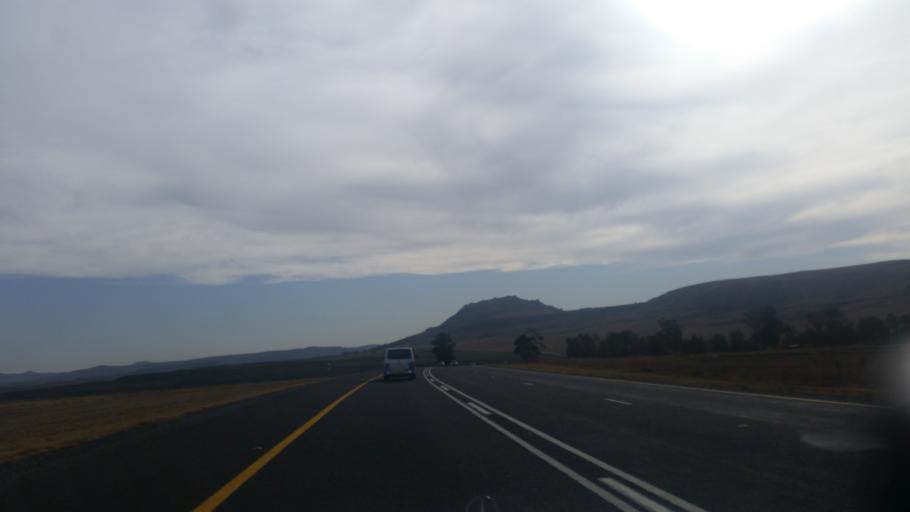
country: ZA
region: Orange Free State
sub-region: Thabo Mofutsanyana District Municipality
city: Phuthaditjhaba
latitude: -28.2956
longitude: 28.8142
